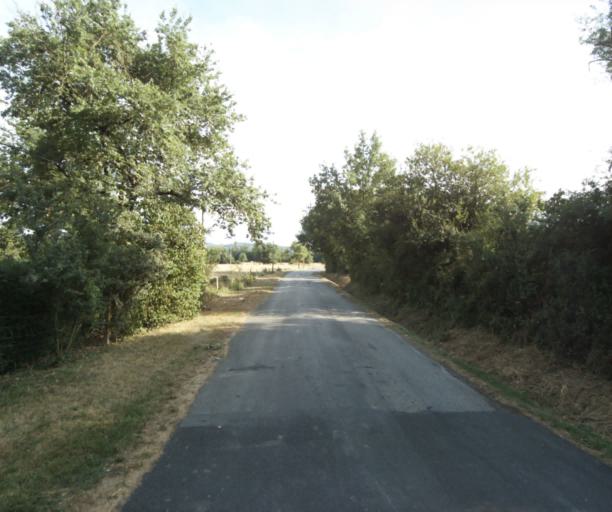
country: FR
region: Midi-Pyrenees
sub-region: Departement de la Haute-Garonne
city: Revel
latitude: 43.4745
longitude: 1.9986
